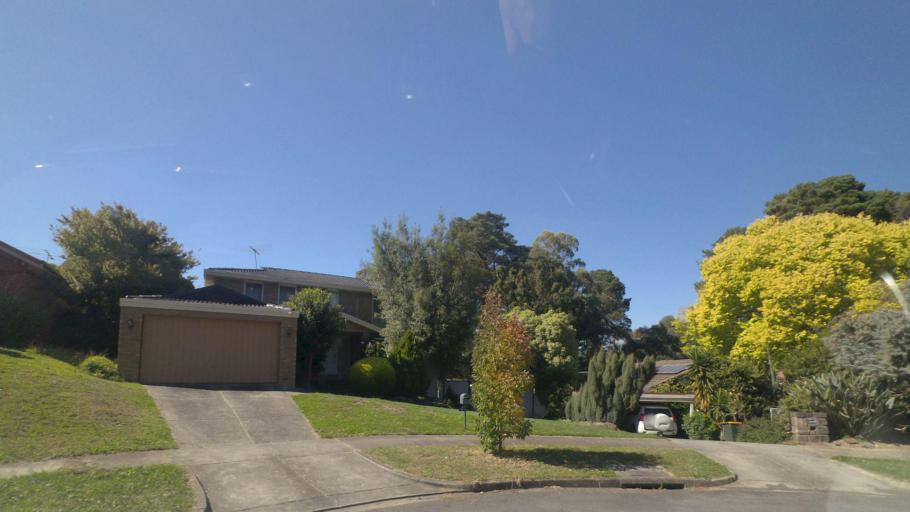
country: AU
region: Victoria
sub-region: Manningham
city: Donvale
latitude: -37.7789
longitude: 145.1750
